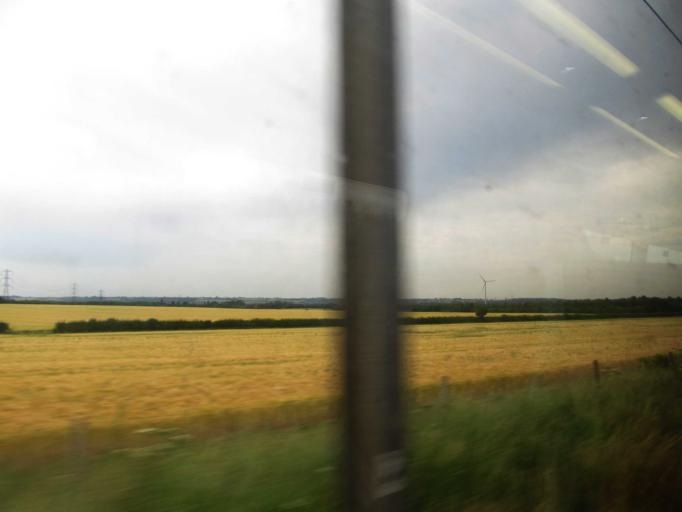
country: GB
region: England
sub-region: Central Bedfordshire
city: Millbrook
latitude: 52.0471
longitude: -0.5149
